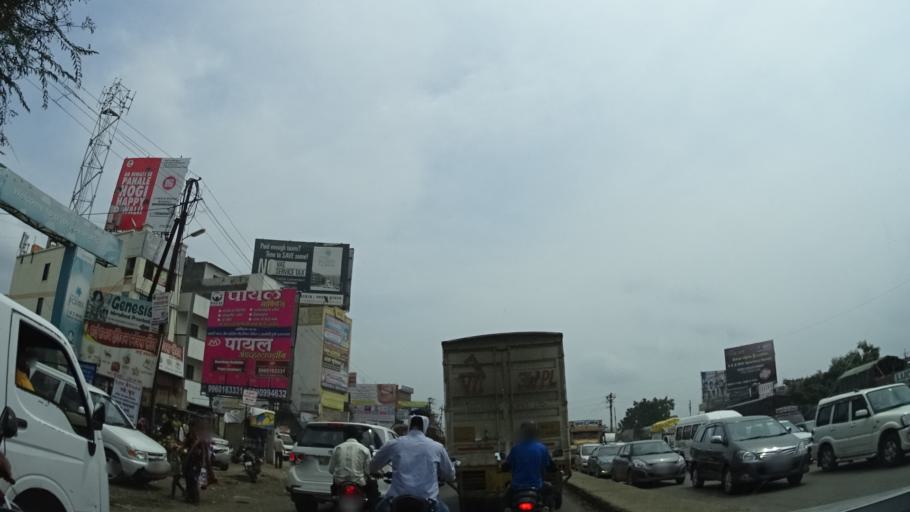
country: IN
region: Maharashtra
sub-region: Pune Division
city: Lohogaon
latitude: 18.5812
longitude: 73.9854
